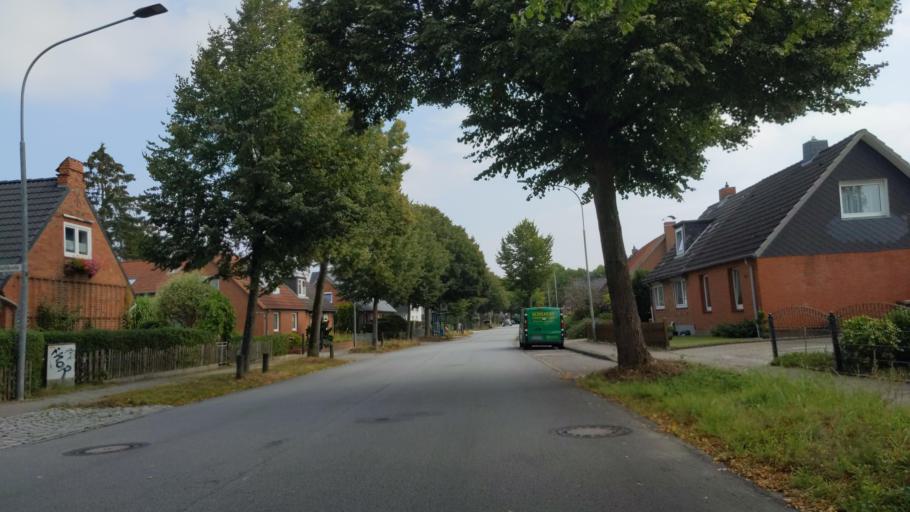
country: DE
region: Schleswig-Holstein
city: Stockelsdorf
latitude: 53.8738
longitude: 10.6296
